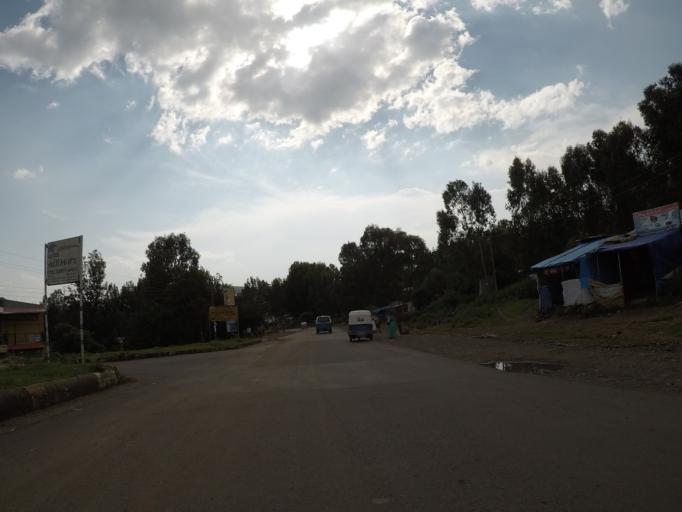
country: ET
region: Amhara
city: Gondar
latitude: 12.5916
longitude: 37.4434
